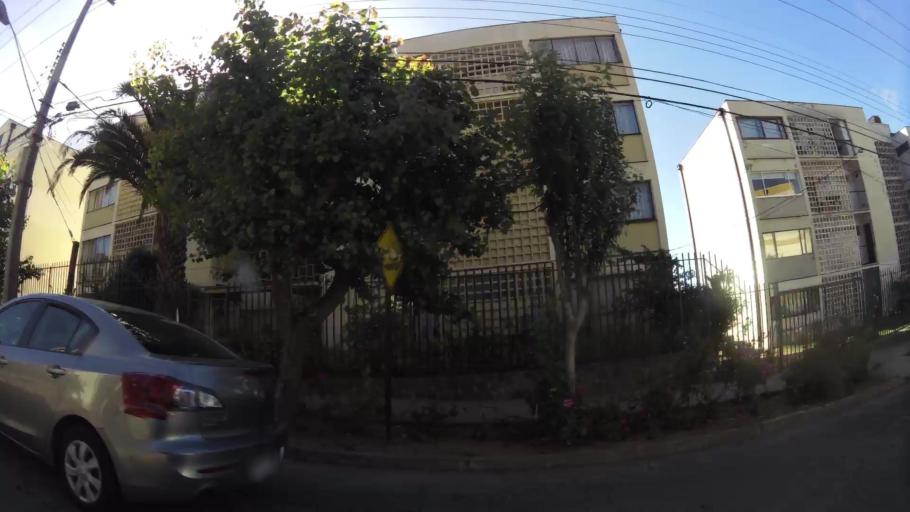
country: CL
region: Valparaiso
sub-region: Provincia de Valparaiso
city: Vina del Mar
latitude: -33.0310
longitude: -71.5576
